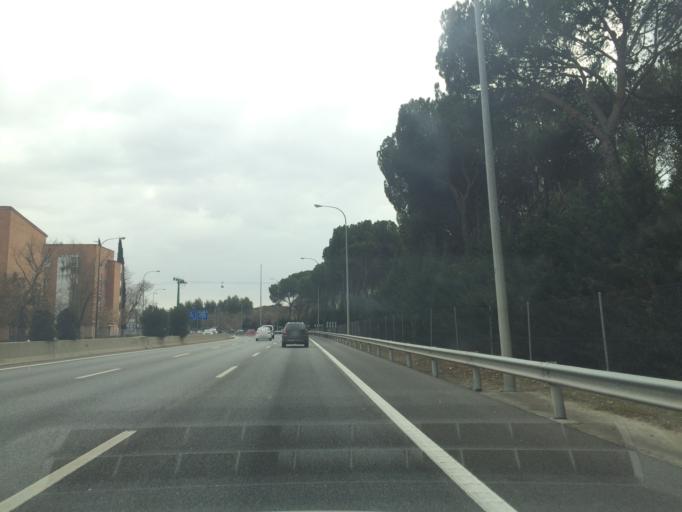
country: ES
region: Madrid
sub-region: Provincia de Madrid
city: Moncloa-Aravaca
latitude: 40.4278
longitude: -3.7352
